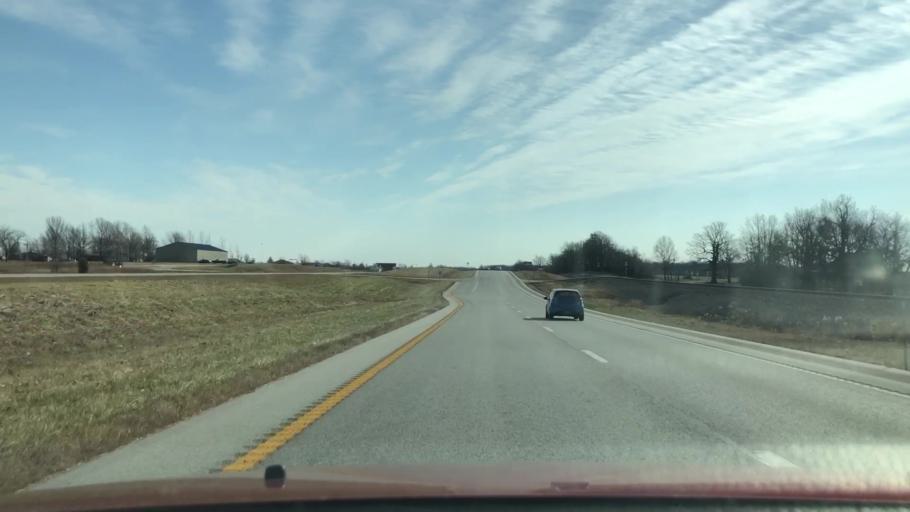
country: US
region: Missouri
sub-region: Webster County
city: Seymour
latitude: 37.1636
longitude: -92.7989
